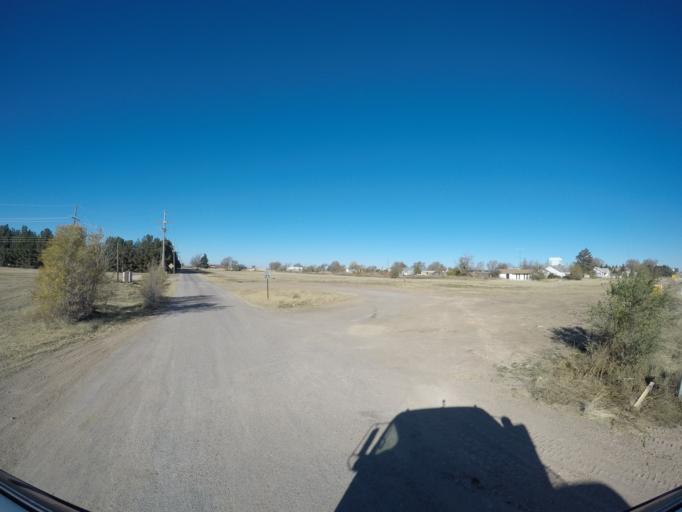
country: US
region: New Mexico
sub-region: Curry County
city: Clovis
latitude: 34.4410
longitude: -103.1968
